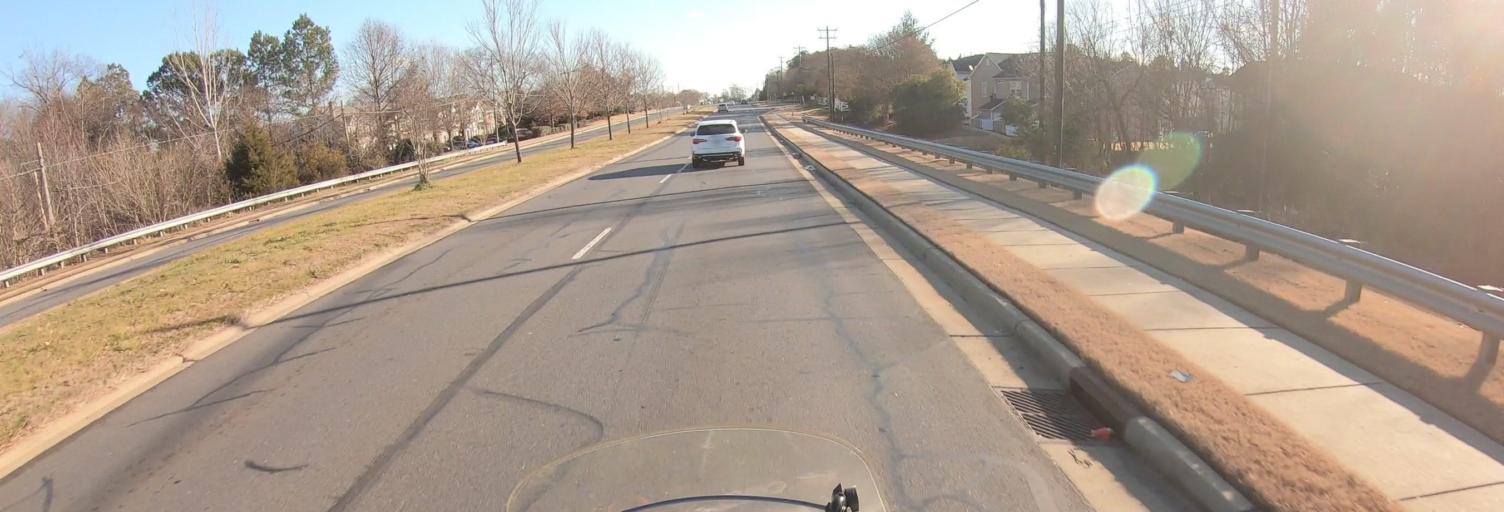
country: US
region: South Carolina
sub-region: York County
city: Lake Wylie
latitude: 35.1127
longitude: -80.9701
